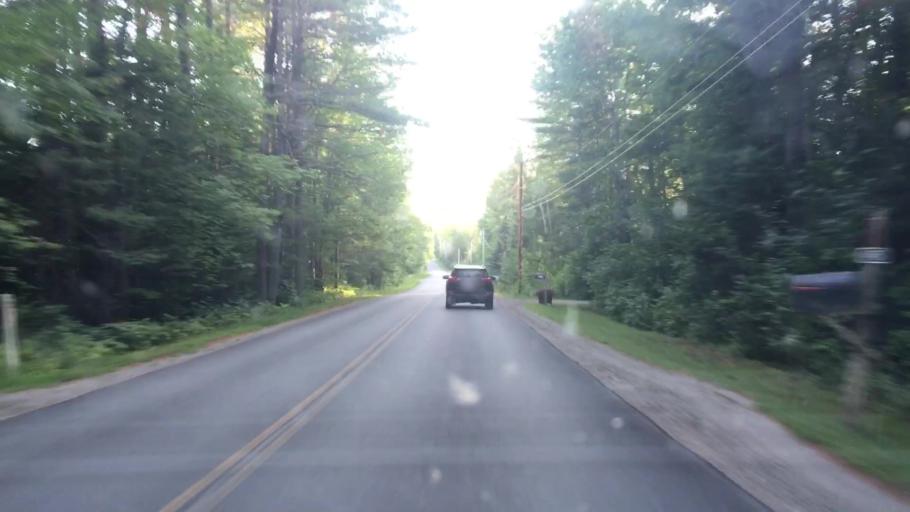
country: US
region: Maine
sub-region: Waldo County
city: Winterport
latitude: 44.6924
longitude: -68.9021
